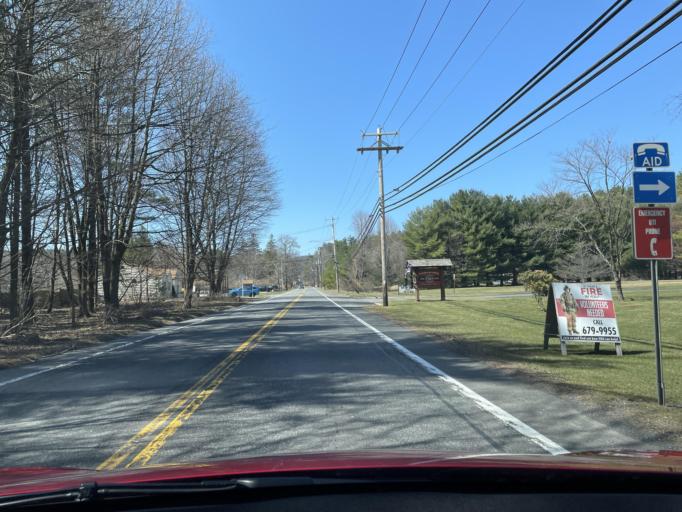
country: US
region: New York
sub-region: Ulster County
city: Woodstock
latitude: 42.0405
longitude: -74.1457
